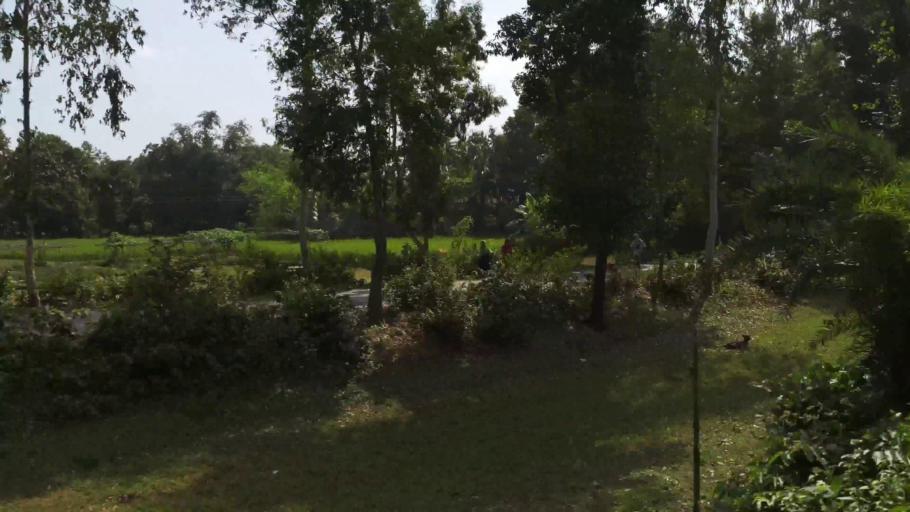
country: BD
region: Dhaka
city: Gafargaon
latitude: 24.1834
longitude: 90.4748
